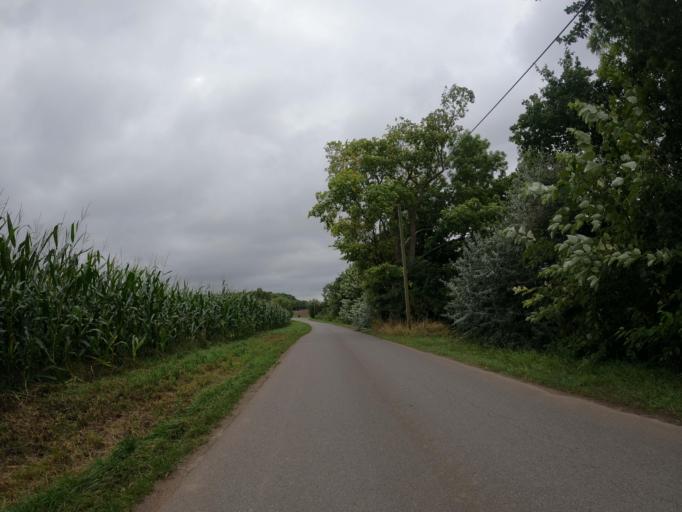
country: DE
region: Mecklenburg-Vorpommern
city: Garz
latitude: 54.3103
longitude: 13.3341
